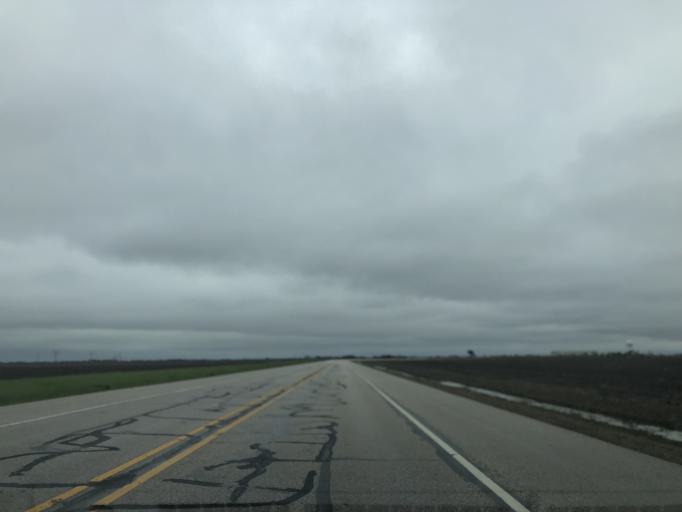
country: US
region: Texas
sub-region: Williamson County
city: Hutto
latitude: 30.6010
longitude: -97.5255
